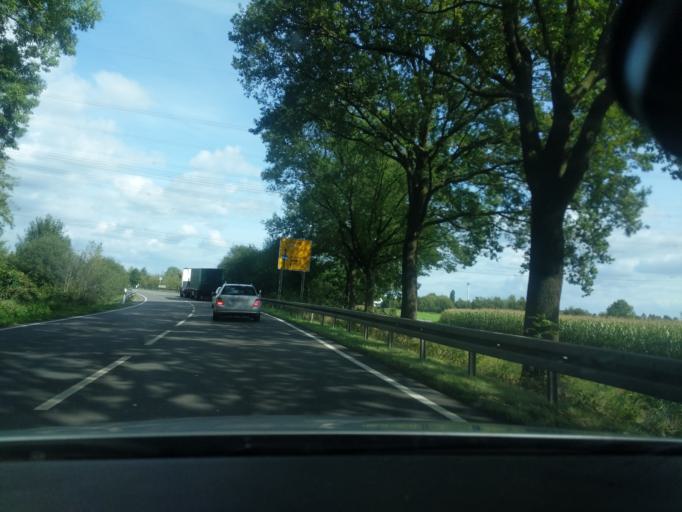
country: DE
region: Lower Saxony
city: Bohmte
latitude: 52.3559
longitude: 8.2964
